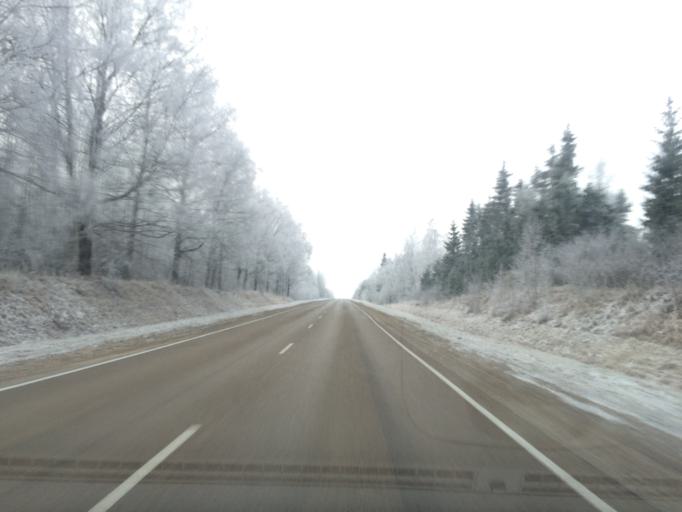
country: LV
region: Rezekne
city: Rezekne
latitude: 56.6223
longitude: 27.4560
